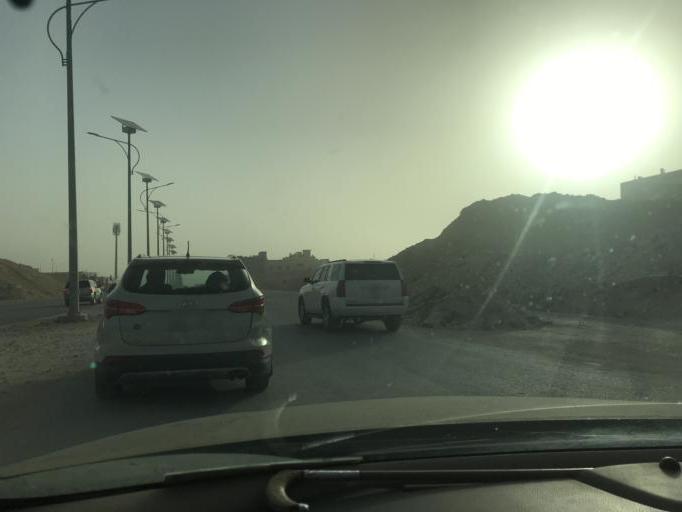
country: SA
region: Ar Riyad
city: Riyadh
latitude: 24.8383
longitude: 46.6681
